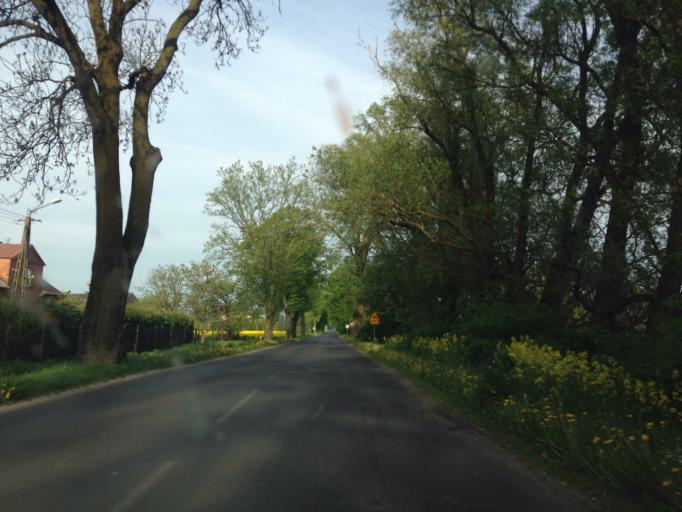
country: PL
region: Kujawsko-Pomorskie
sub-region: Powiat wabrzeski
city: Pluznica
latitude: 53.2916
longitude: 18.7847
